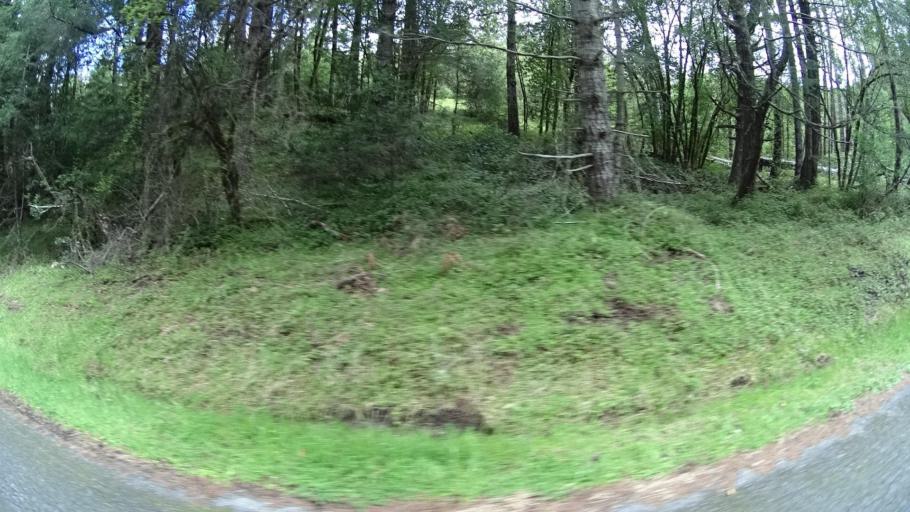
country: US
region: California
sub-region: Humboldt County
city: Blue Lake
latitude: 40.7960
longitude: -123.9803
